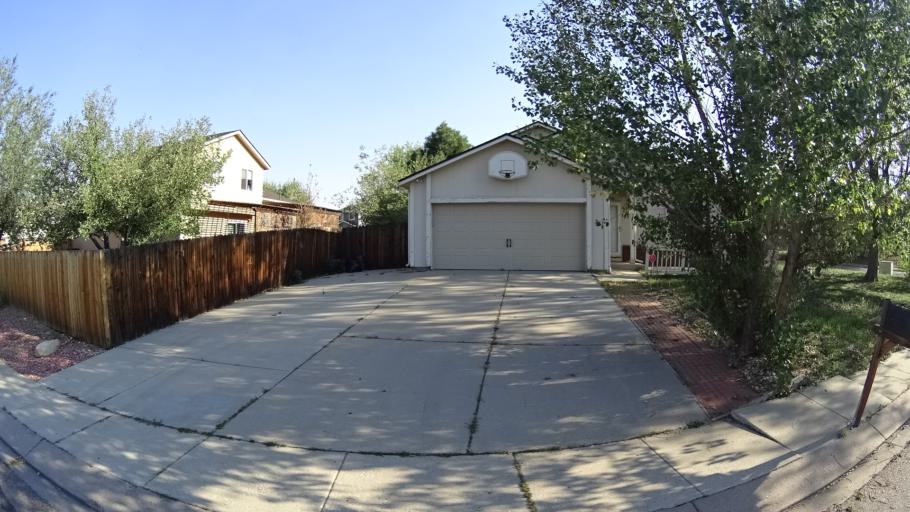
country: US
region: Colorado
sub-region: El Paso County
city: Stratmoor
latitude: 38.7735
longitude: -104.8007
